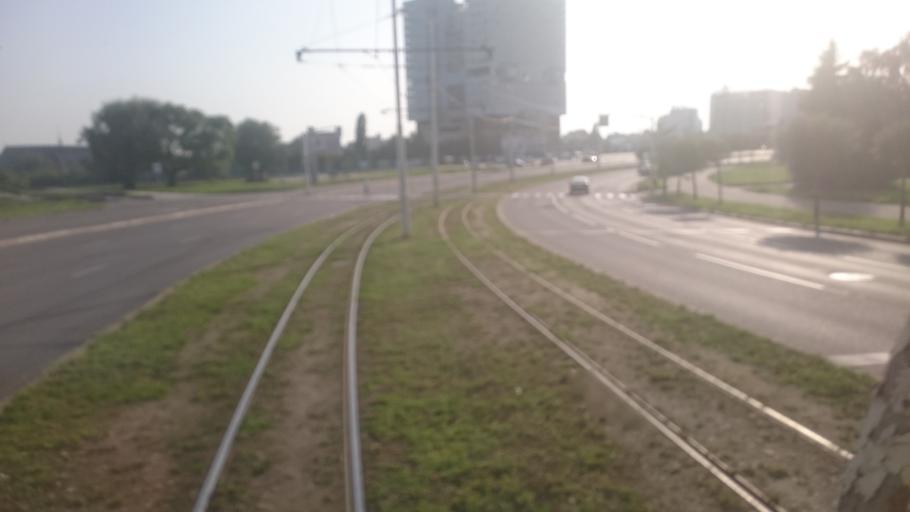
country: RU
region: Kaliningrad
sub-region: Gorod Kaliningrad
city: Kaliningrad
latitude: 54.7110
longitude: 20.5166
